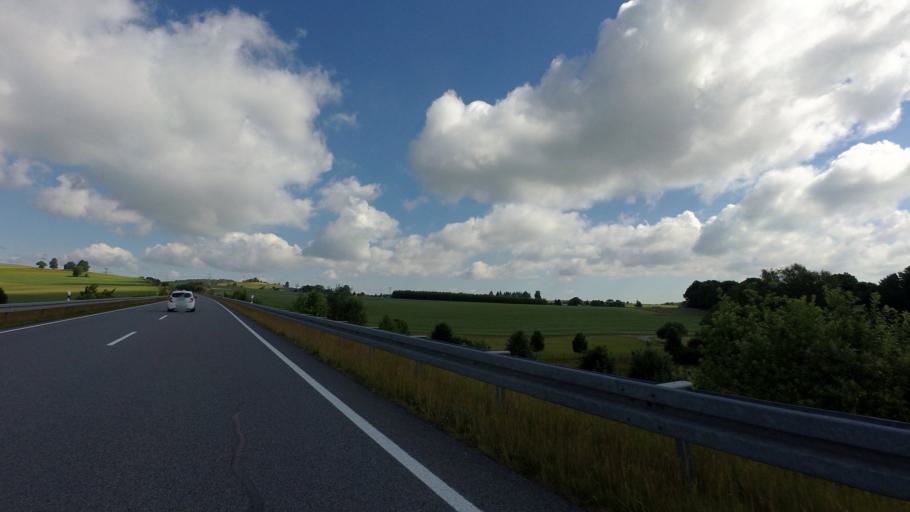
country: DE
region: Saxony
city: Berthelsdorf
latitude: 51.0686
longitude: 14.1977
